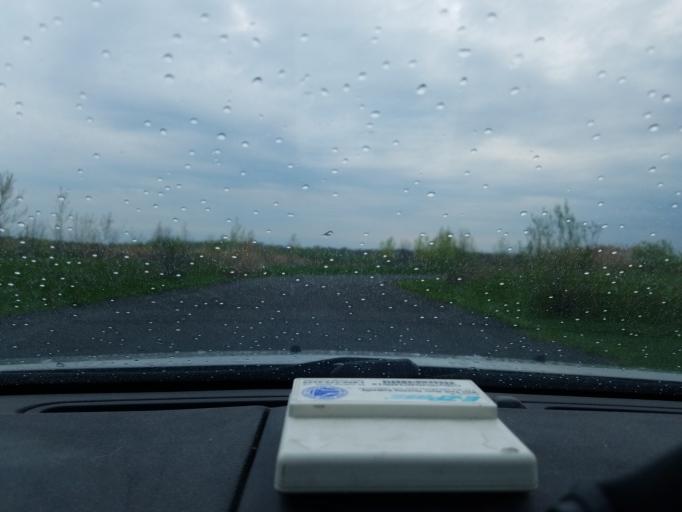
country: US
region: New York
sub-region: Onondaga County
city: East Syracuse
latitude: 43.1057
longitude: -76.0875
